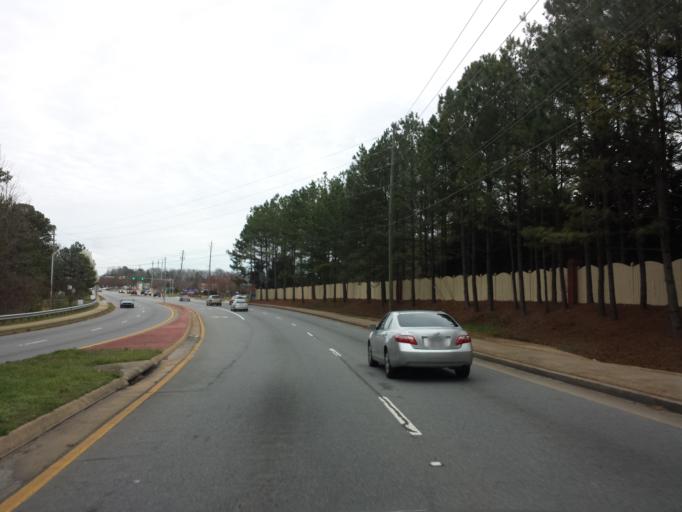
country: US
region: Georgia
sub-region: Cherokee County
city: Woodstock
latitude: 34.0381
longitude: -84.4696
